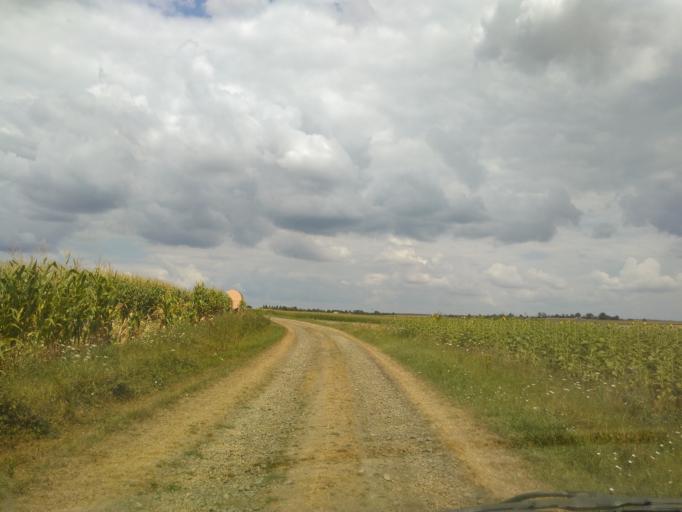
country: FR
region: Pays de la Loire
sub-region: Departement de la Vendee
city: Sainte-Hermine
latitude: 46.5637
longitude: -1.0248
